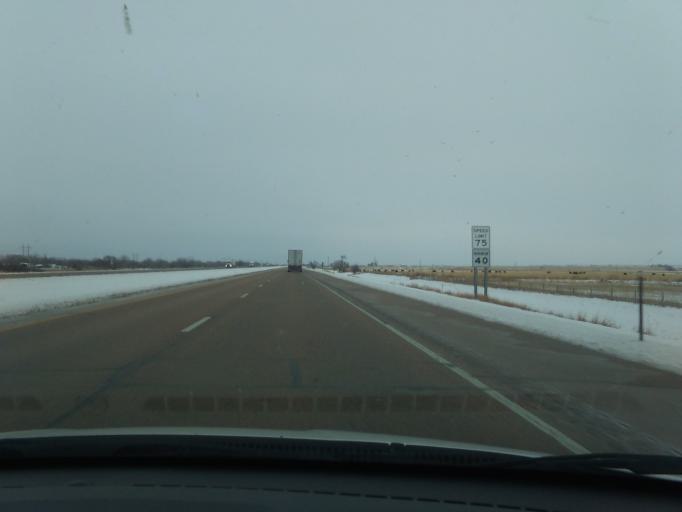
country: US
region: Nebraska
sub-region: Keith County
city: Ogallala
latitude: 41.0817
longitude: -101.8757
